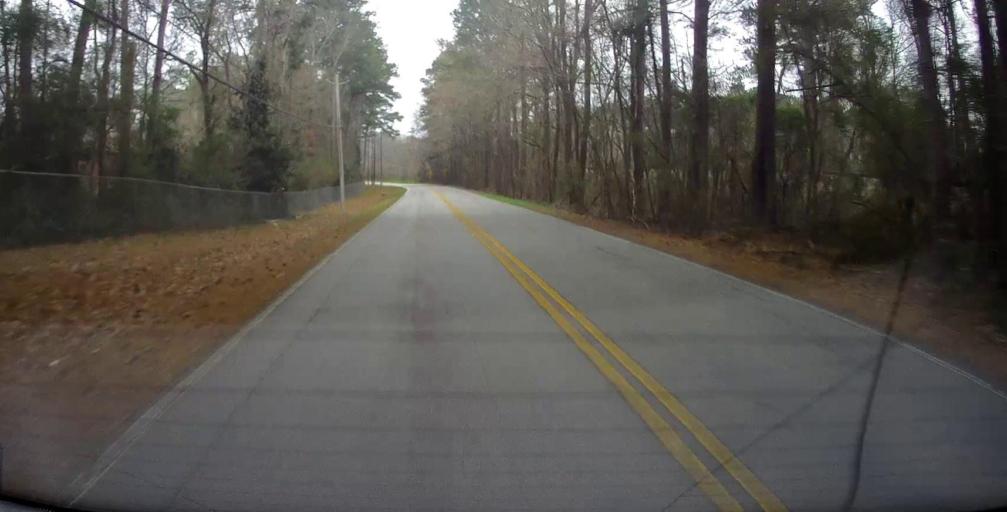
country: US
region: Georgia
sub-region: Bibb County
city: Macon
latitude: 32.8820
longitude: -83.7248
